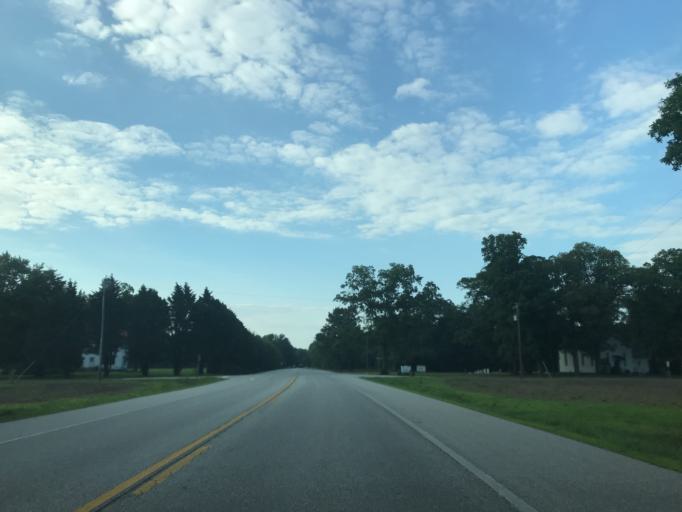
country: US
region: Maryland
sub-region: Caroline County
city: Federalsburg
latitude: 38.7547
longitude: -75.7902
